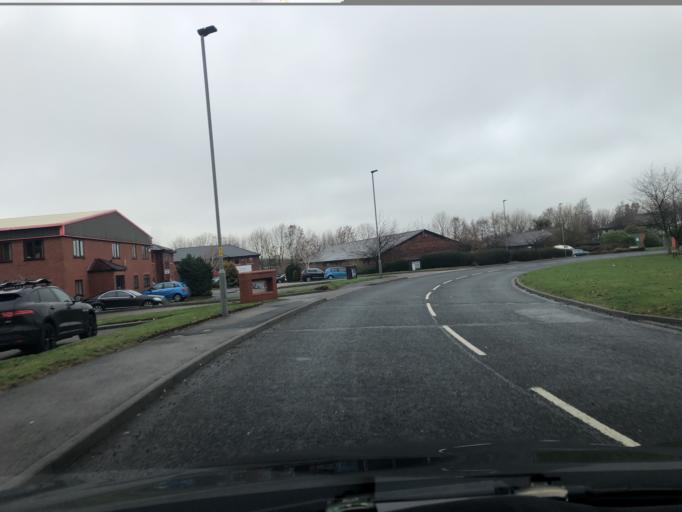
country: GB
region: England
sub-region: North Yorkshire
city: Stokesley
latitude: 54.4625
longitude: -1.1780
